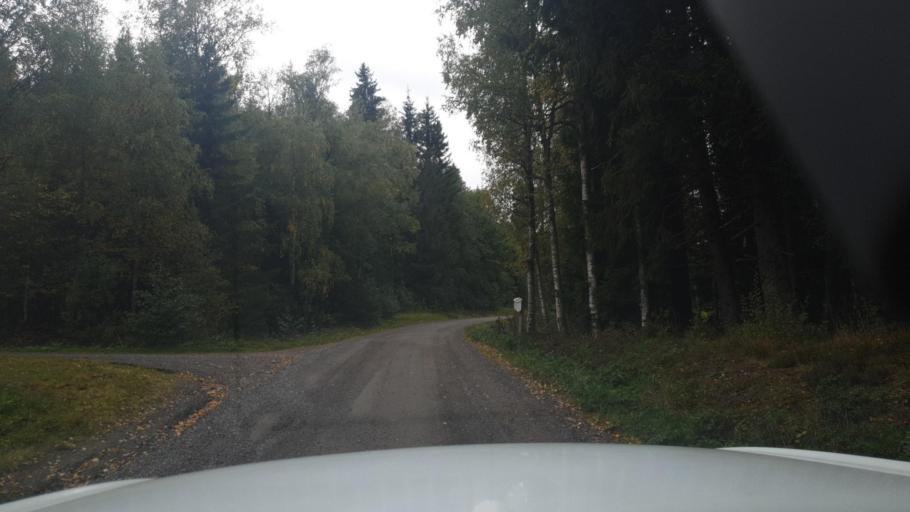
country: SE
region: Vaermland
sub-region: Torsby Kommun
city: Torsby
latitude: 60.1866
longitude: 12.6637
